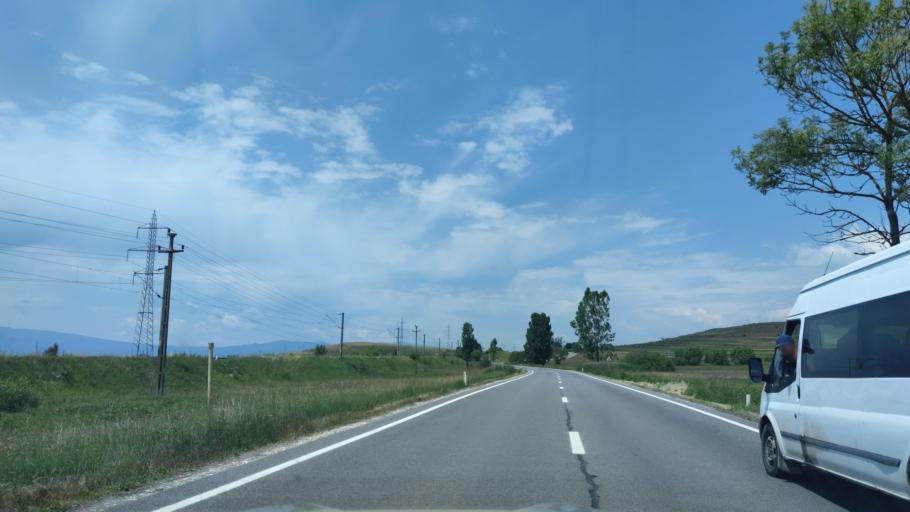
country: RO
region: Harghita
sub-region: Comuna Suseni
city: Valea Stramba
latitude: 46.6768
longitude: 25.6006
